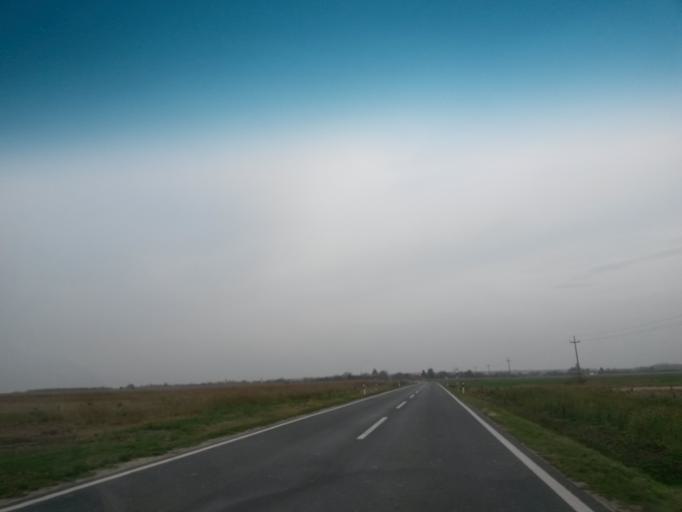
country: HR
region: Vukovarsko-Srijemska
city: Slakovci
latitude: 45.2166
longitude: 18.9682
